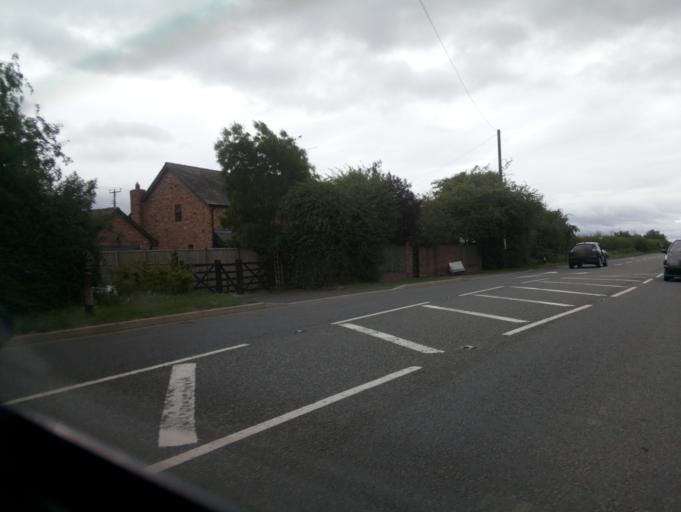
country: GB
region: England
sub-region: Worcestershire
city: Kempsey
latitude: 52.1605
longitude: -2.2157
